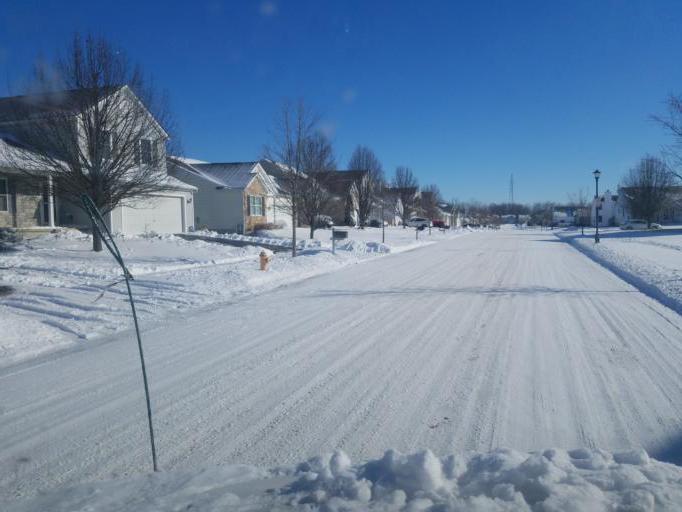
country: US
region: Ohio
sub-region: Franklin County
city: Worthington
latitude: 40.1456
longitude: -83.0136
